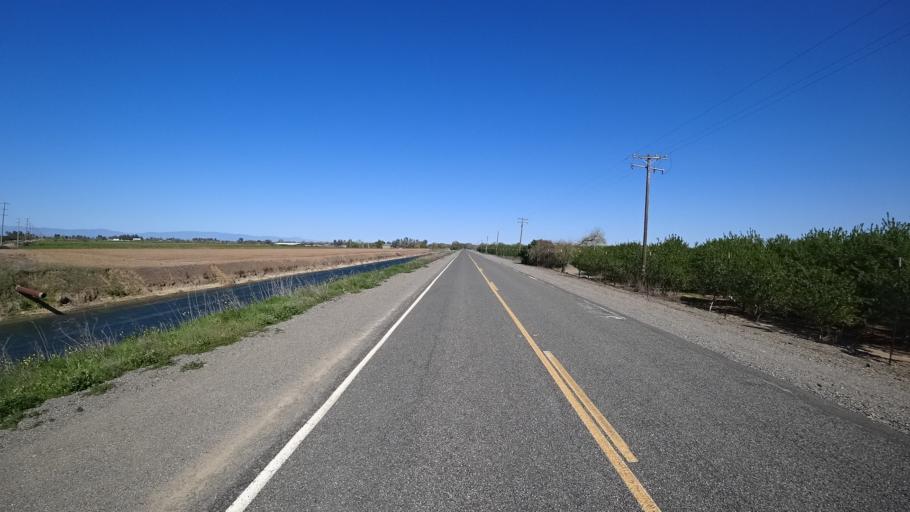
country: US
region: California
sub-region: Glenn County
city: Hamilton City
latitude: 39.7758
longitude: -122.0388
